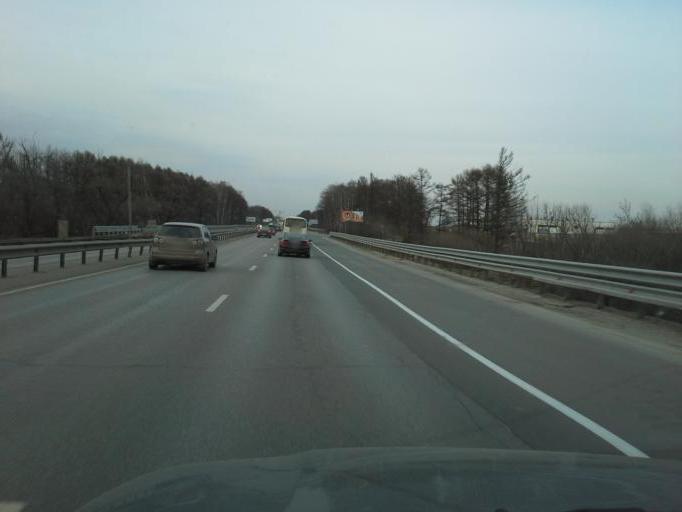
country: RU
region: Moscow
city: Novo-Peredelkino
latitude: 55.6826
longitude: 37.3256
